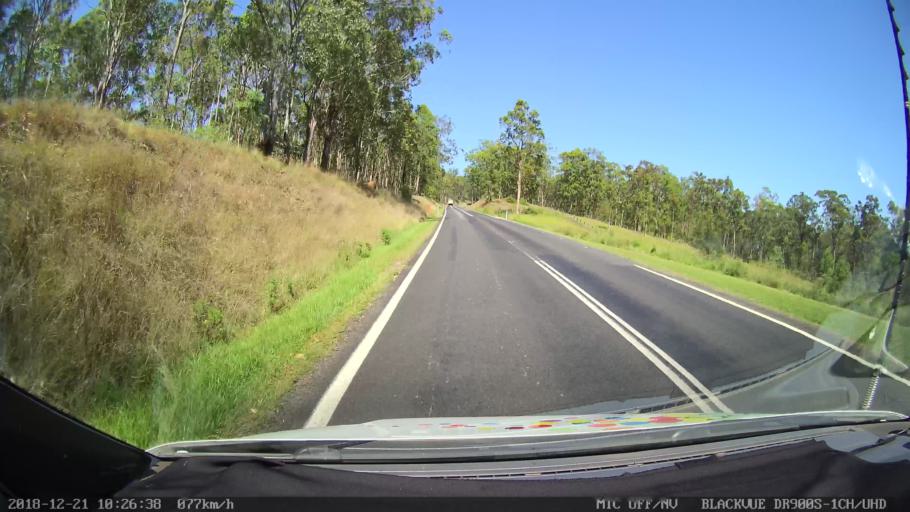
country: AU
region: New South Wales
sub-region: Clarence Valley
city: South Grafton
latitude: -29.6301
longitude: 152.7482
